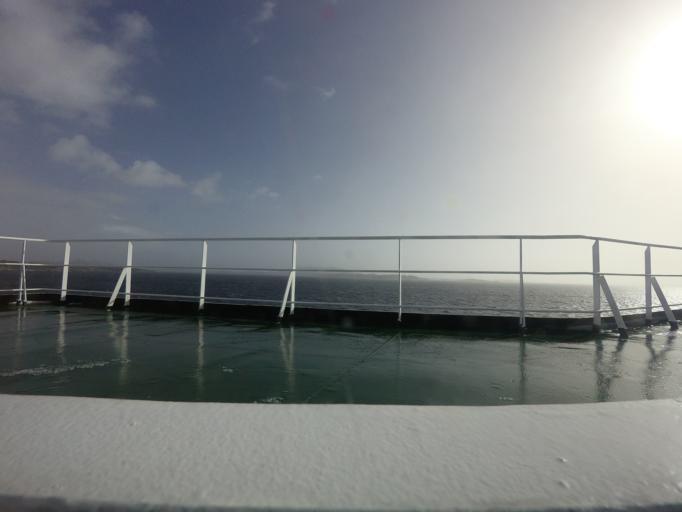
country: NO
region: Hordaland
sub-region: Oygarden
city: Tjeldsto
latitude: 60.6365
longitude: 4.9125
